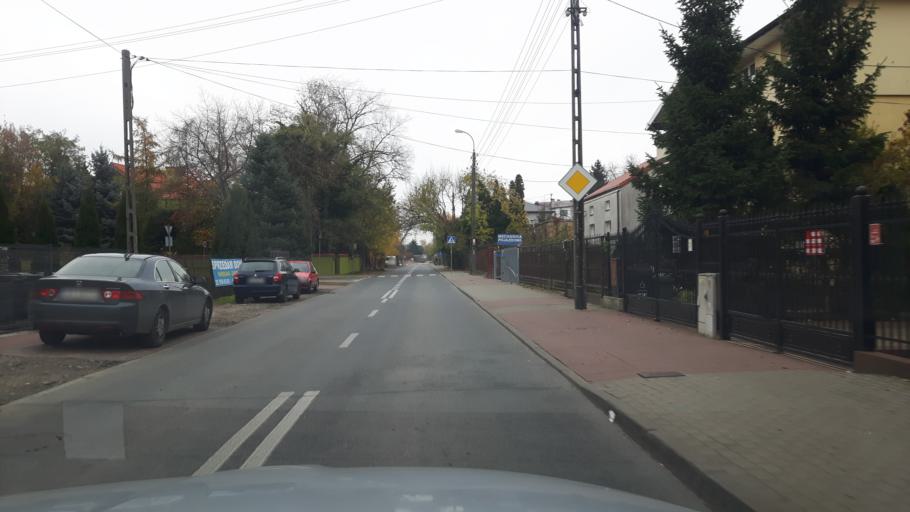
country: PL
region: Masovian Voivodeship
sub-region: Warszawa
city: Targowek
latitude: 52.2796
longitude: 21.0743
